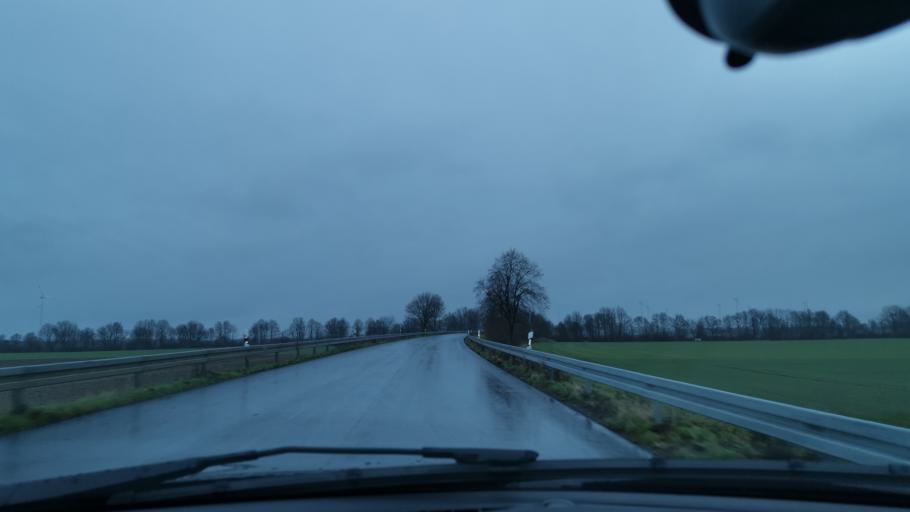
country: DE
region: North Rhine-Westphalia
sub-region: Regierungsbezirk Koln
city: Bedburg
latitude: 51.0086
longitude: 6.4992
